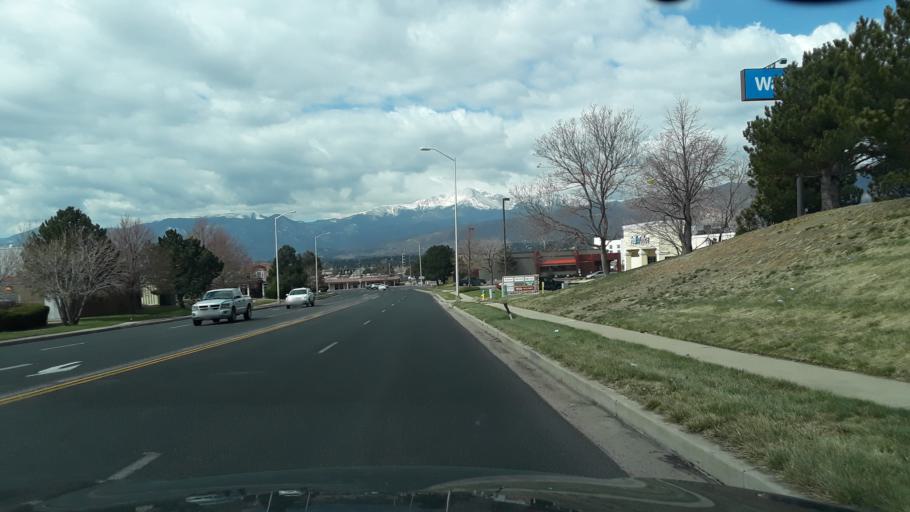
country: US
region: Colorado
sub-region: El Paso County
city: Air Force Academy
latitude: 38.9482
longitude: -104.8000
